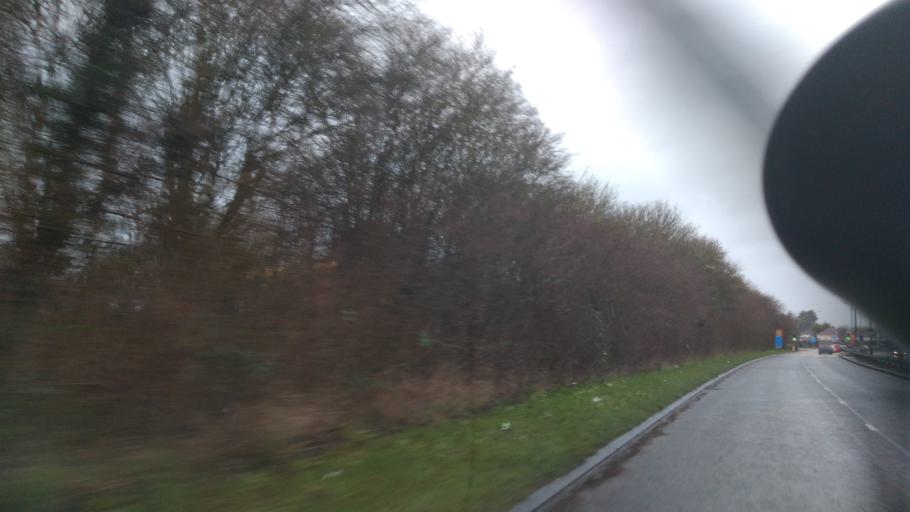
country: GB
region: England
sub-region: Borough of Swindon
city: Swindon
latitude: 51.5783
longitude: -1.7749
